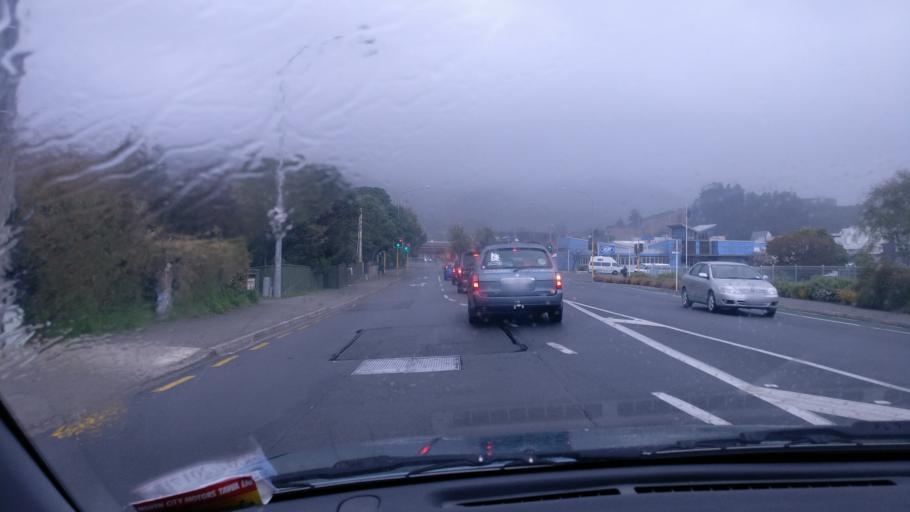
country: NZ
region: Wellington
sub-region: Kapiti Coast District
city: Paraparaumu
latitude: -40.9137
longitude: 175.0049
